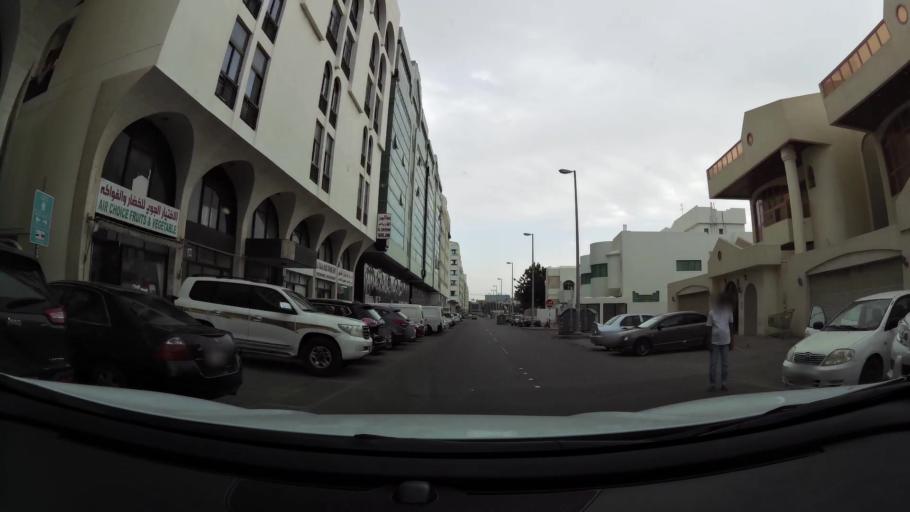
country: AE
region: Abu Dhabi
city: Abu Dhabi
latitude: 24.4810
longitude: 54.3773
